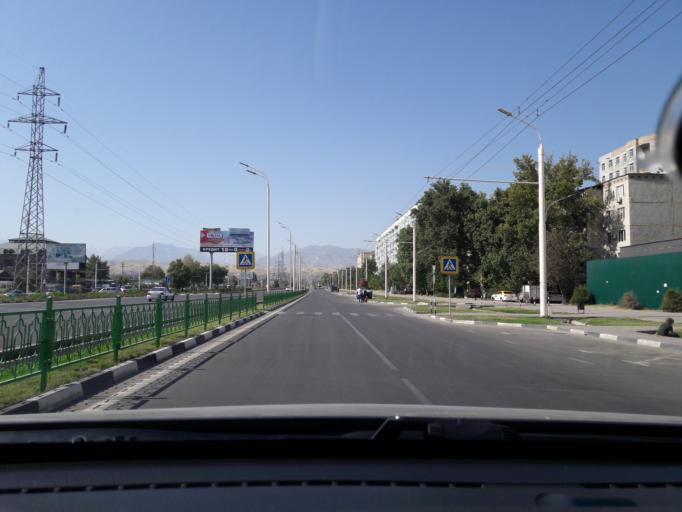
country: TJ
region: Dushanbe
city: Dushanbe
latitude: 38.5525
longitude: 68.7416
